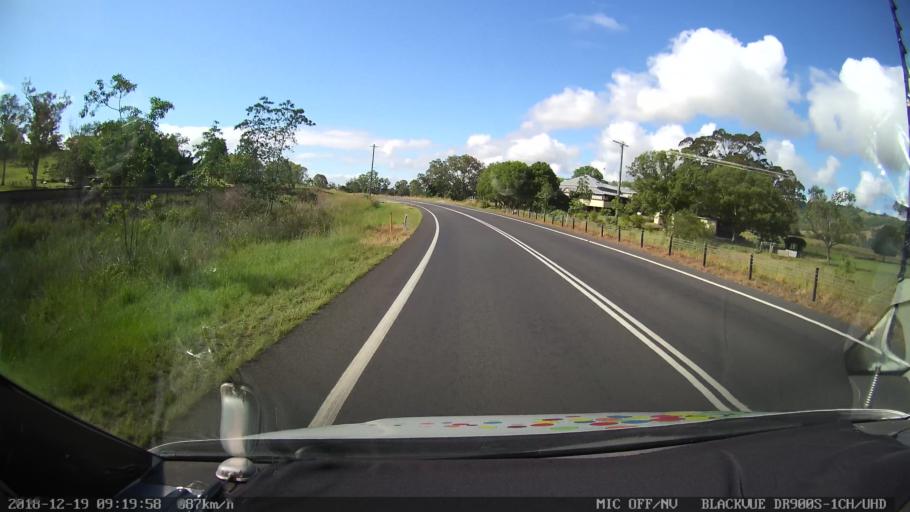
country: AU
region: New South Wales
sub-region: Kyogle
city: Kyogle
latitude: -28.5668
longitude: 152.9778
